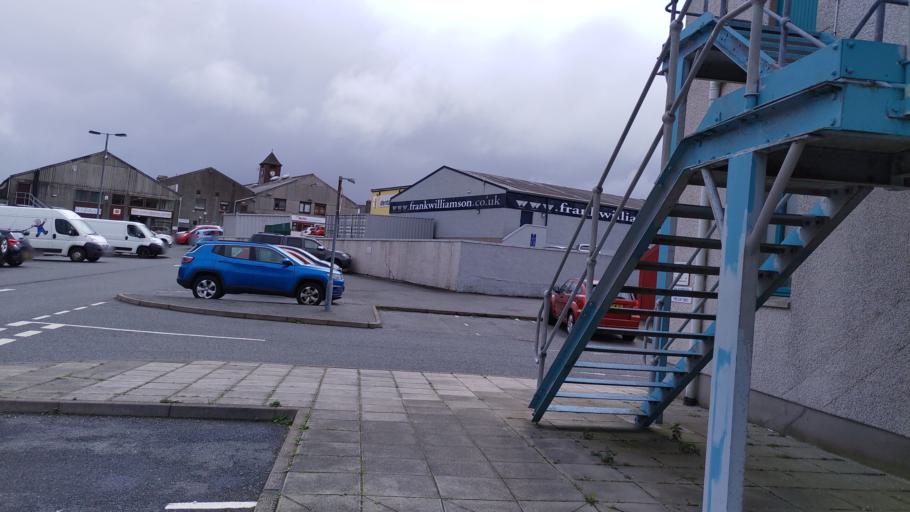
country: GB
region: Scotland
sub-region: Shetland Islands
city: Lerwick
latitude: 60.1582
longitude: -1.1564
